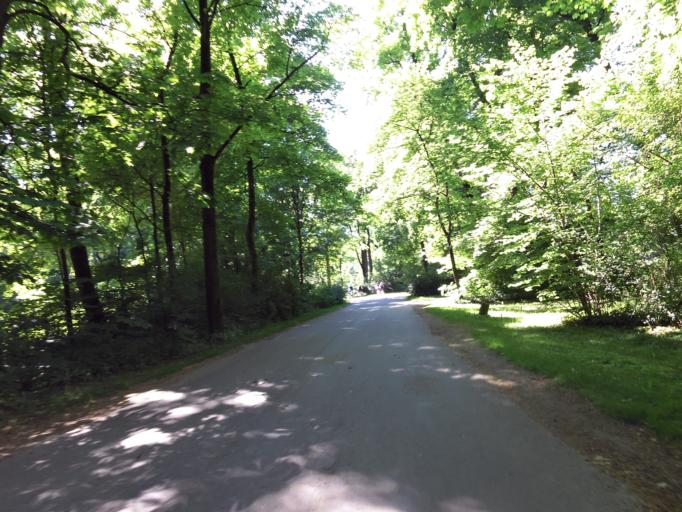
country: DE
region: Bavaria
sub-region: Upper Bavaria
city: Bogenhausen
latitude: 48.1551
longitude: 11.5985
